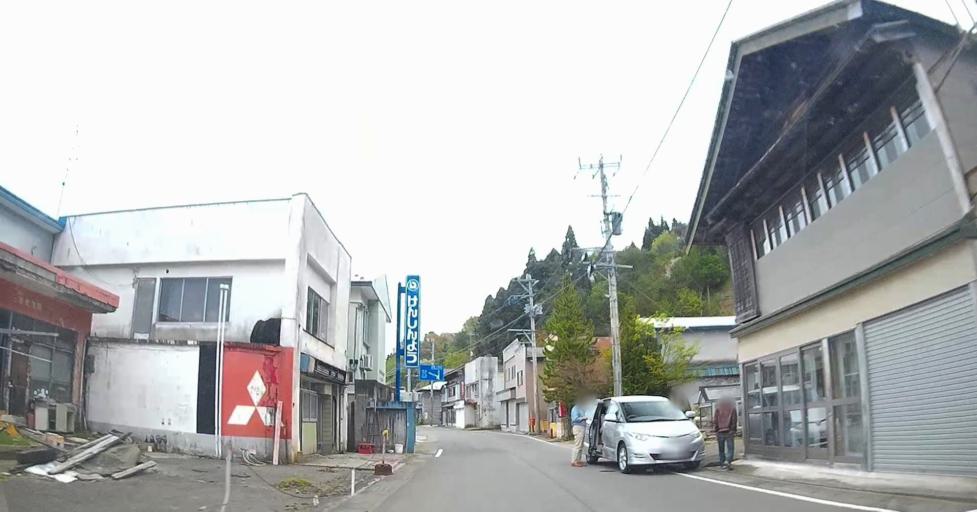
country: JP
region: Aomori
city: Shimokizukuri
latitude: 41.1969
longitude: 140.4301
